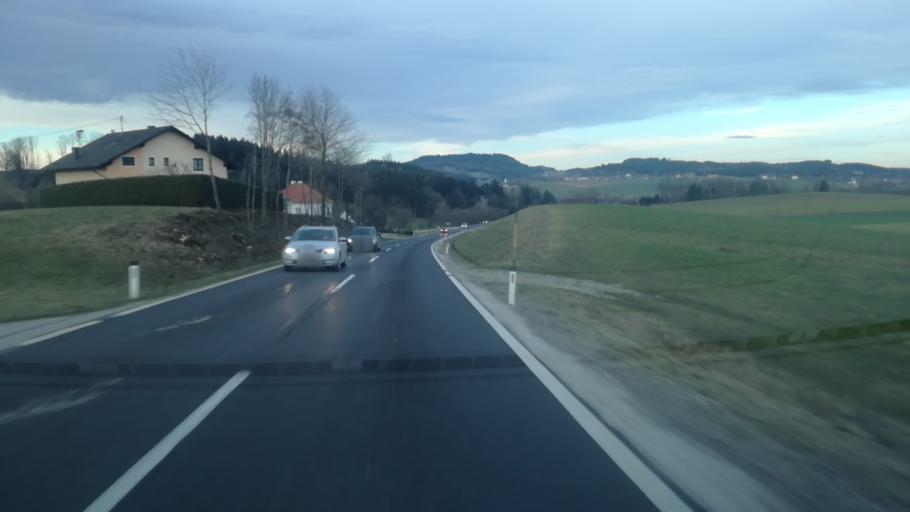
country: AT
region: Upper Austria
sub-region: Politischer Bezirk Ried im Innkreis
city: Waldzell
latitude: 48.1573
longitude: 13.4340
